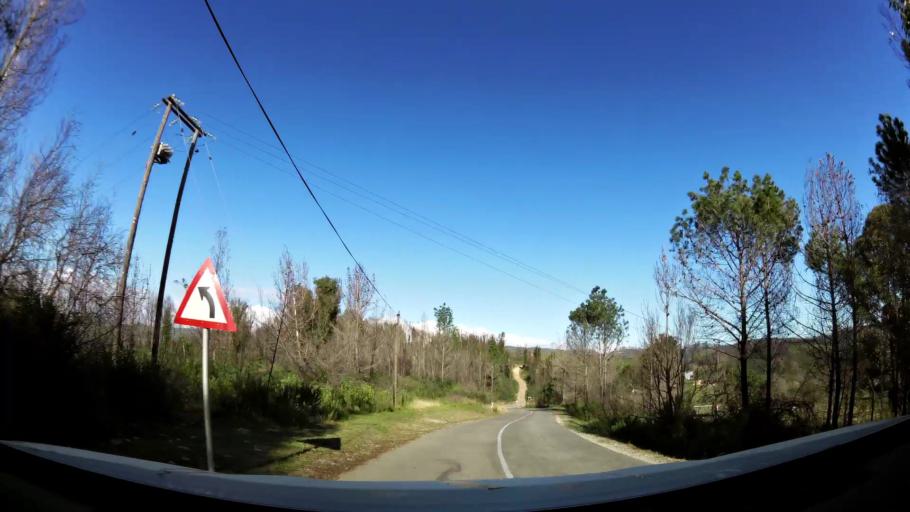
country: ZA
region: Western Cape
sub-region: Eden District Municipality
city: Knysna
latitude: -34.0233
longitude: 23.0086
